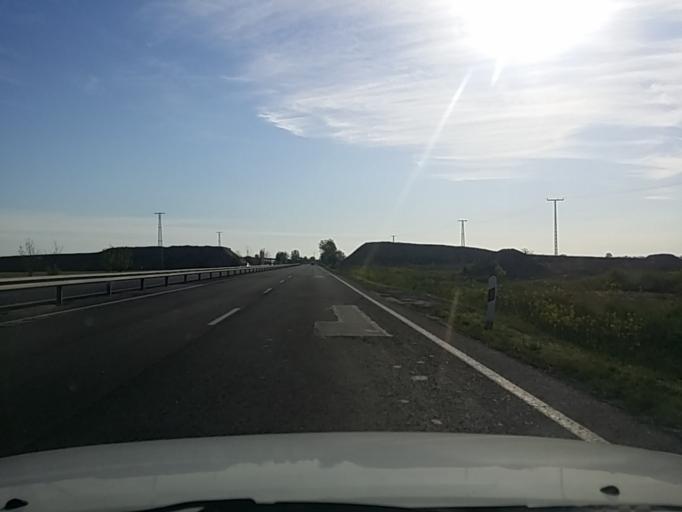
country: HU
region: Jasz-Nagykun-Szolnok
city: Tiszapuspoki
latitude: 47.1813
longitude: 20.3510
